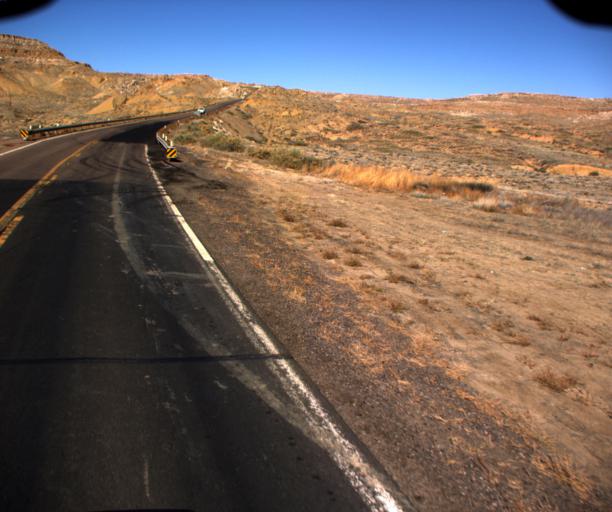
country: US
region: Arizona
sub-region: Navajo County
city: First Mesa
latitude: 35.7964
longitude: -110.5124
